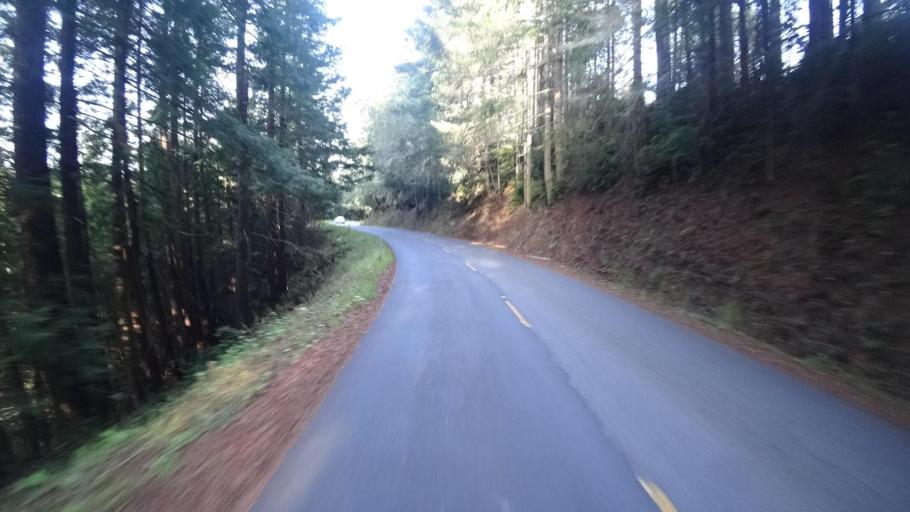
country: US
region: California
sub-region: Humboldt County
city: Bayside
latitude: 40.7567
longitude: -124.0330
